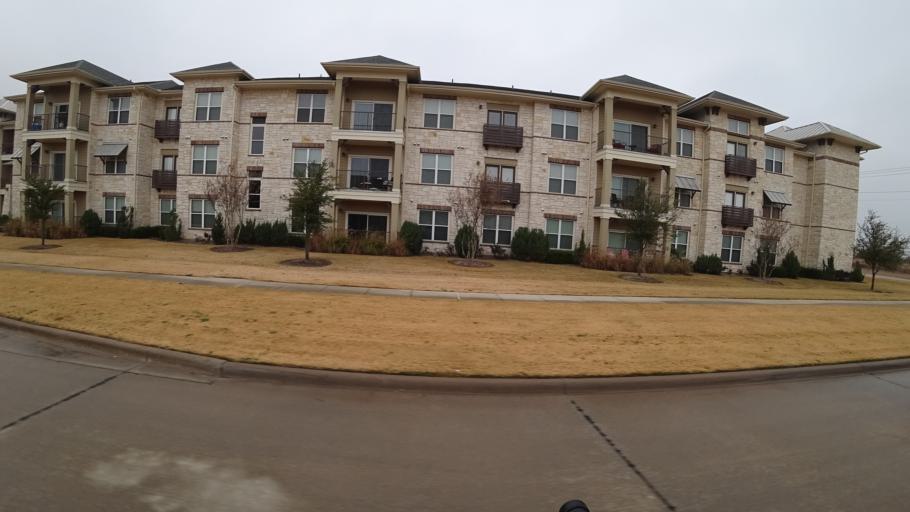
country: US
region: Texas
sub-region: Denton County
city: The Colony
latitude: 33.0645
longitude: -96.9149
